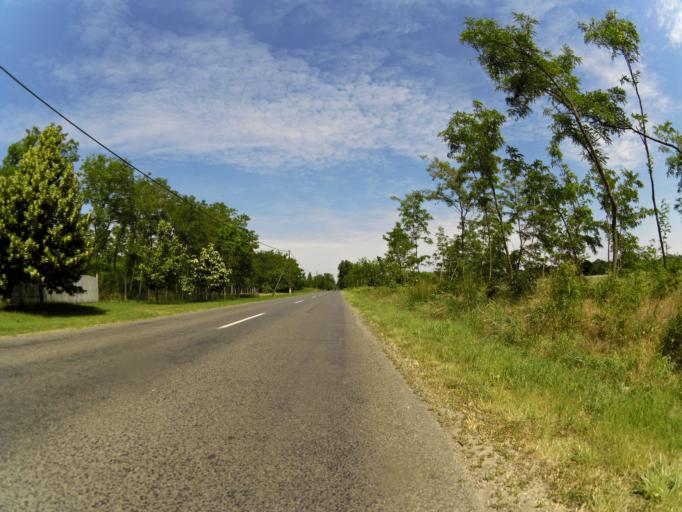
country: HU
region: Csongrad
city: Sandorfalva
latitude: 46.4043
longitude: 20.1136
